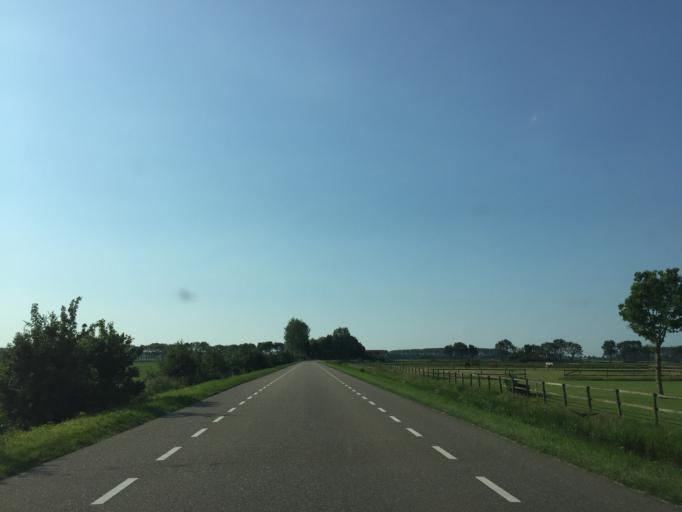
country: NL
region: Gelderland
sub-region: Gemeente Tiel
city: Tiel
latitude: 51.8594
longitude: 5.4872
